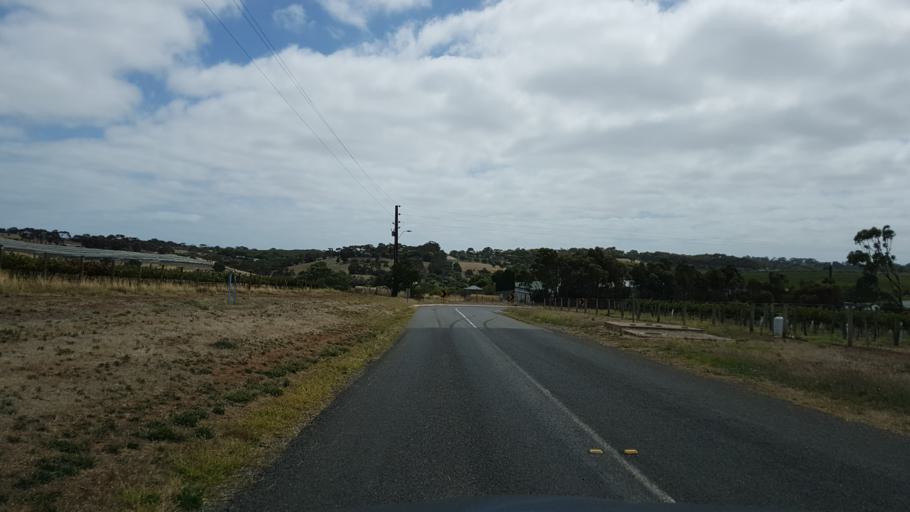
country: AU
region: South Australia
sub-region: Onkaparinga
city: McLaren Vale
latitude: -35.2114
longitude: 138.5174
